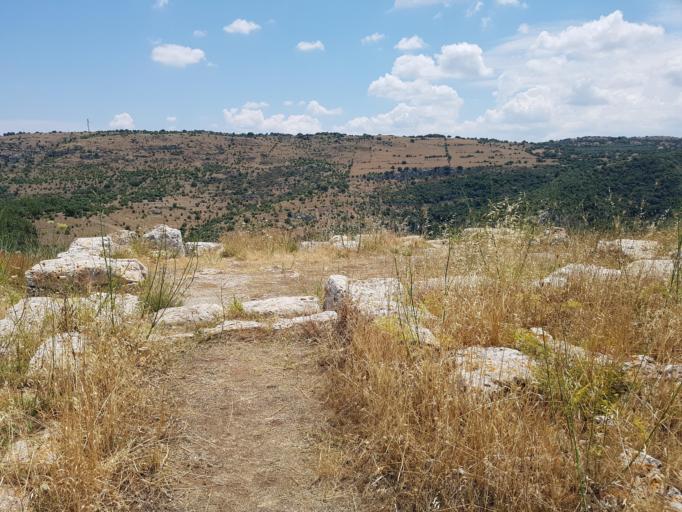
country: IT
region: Sicily
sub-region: Provincia di Siracusa
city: Sortino
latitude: 37.1594
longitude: 15.0267
